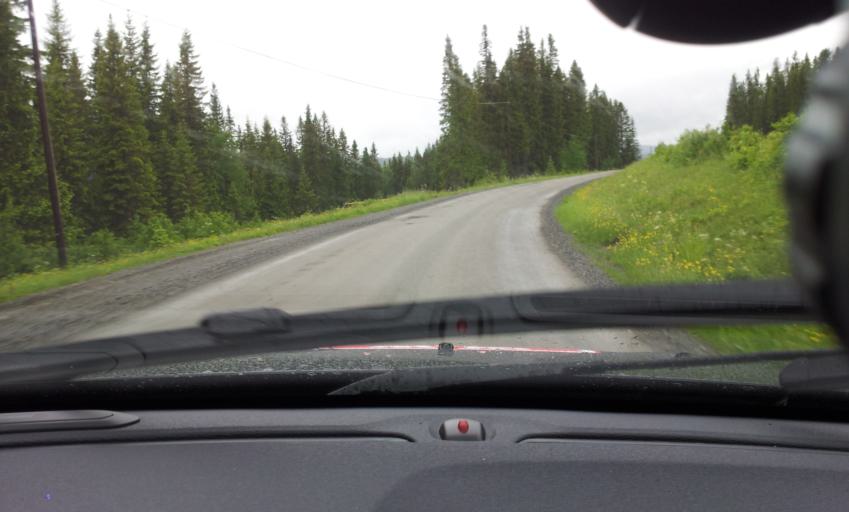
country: SE
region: Jaemtland
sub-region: Are Kommun
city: Are
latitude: 63.4262
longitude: 12.8095
